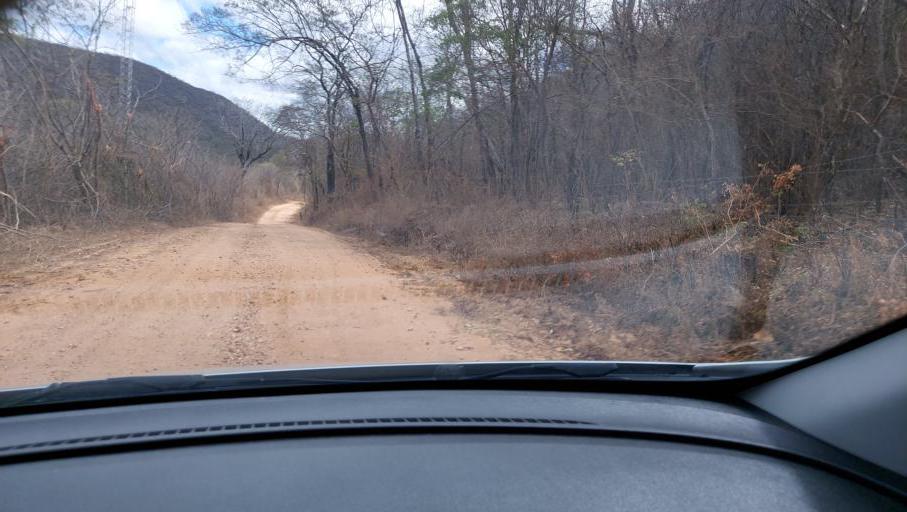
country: BR
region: Bahia
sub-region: Oliveira Dos Brejinhos
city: Beira Rio
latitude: -12.0823
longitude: -42.5433
